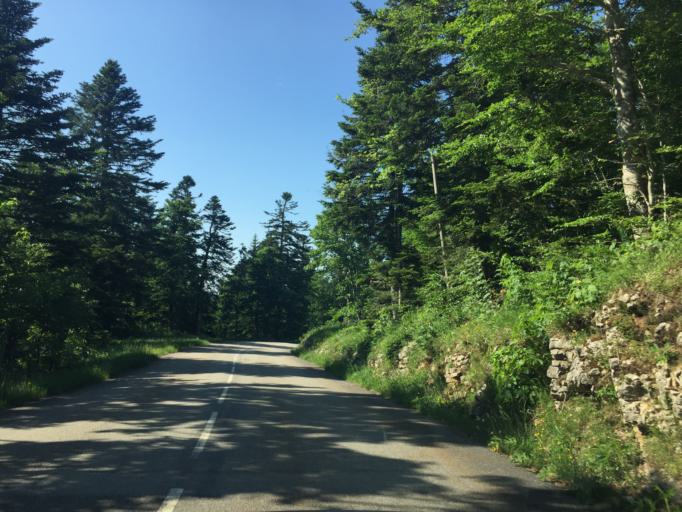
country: FR
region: Rhone-Alpes
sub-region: Departement de la Drome
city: Saint-Jean-en-Royans
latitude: 44.9154
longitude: 5.3251
